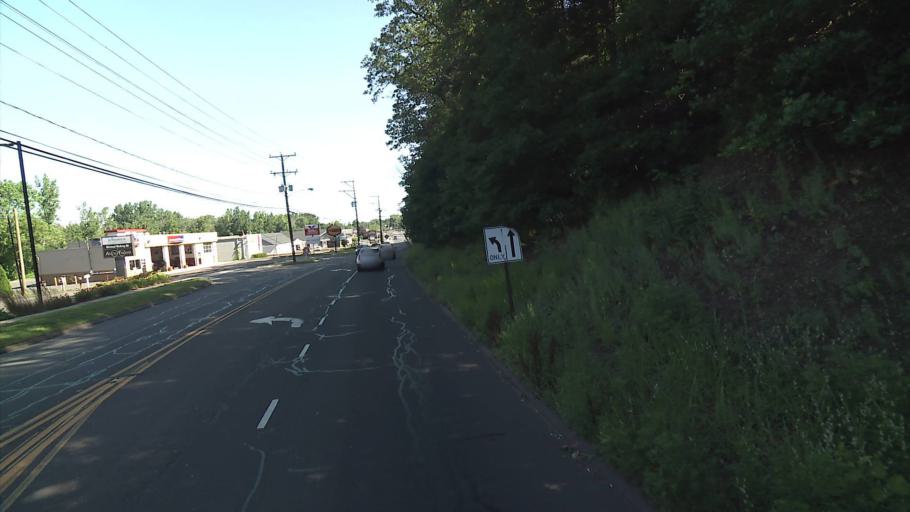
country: US
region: Connecticut
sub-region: Hartford County
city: Plainville
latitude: 41.6184
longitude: -72.8739
